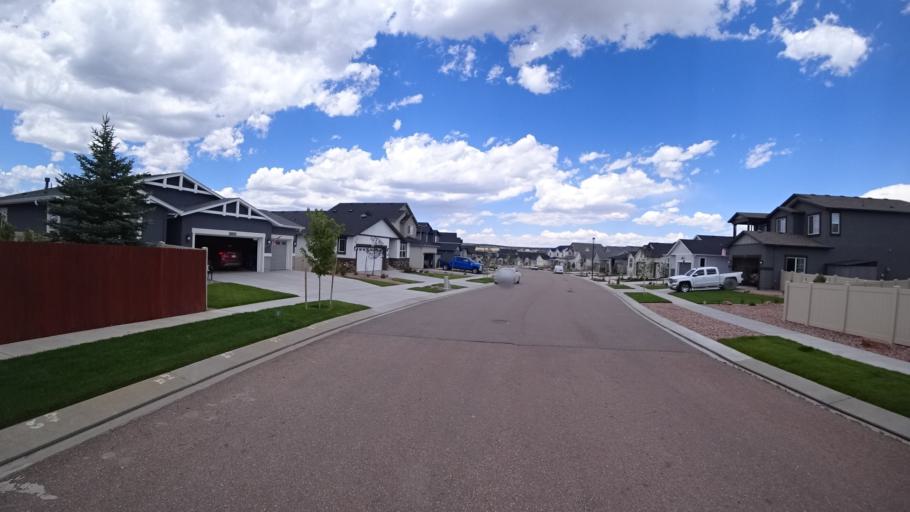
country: US
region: Colorado
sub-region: El Paso County
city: Black Forest
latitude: 38.9470
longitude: -104.7086
